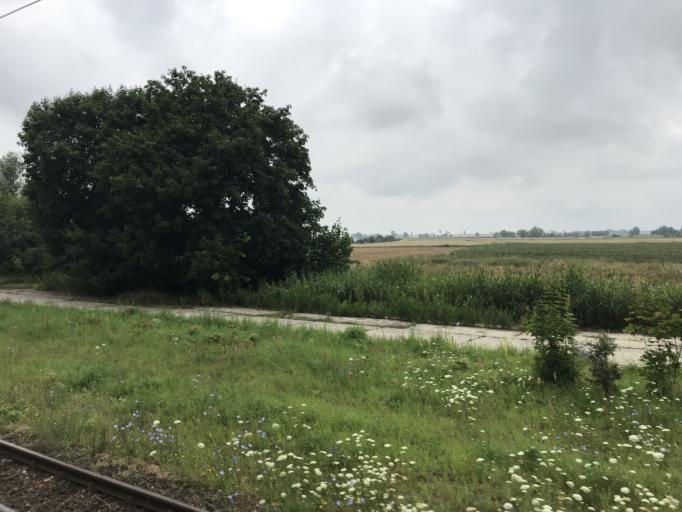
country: PL
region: Warmian-Masurian Voivodeship
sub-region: Powiat elblaski
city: Gronowo Elblaskie
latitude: 54.0904
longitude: 19.3071
